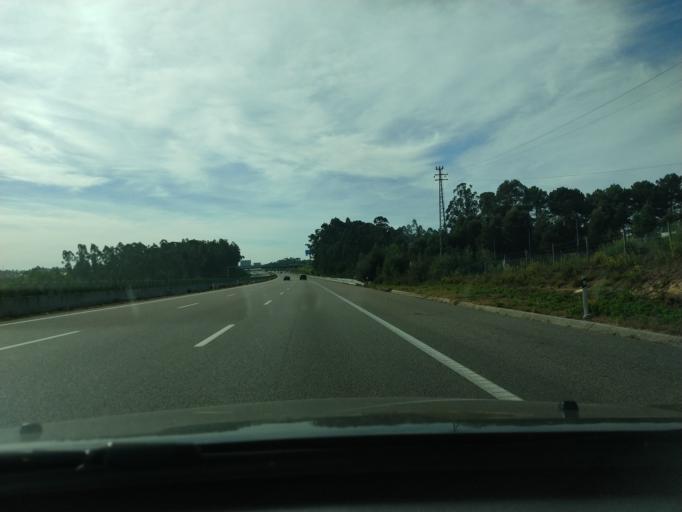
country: PT
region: Aveiro
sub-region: Santa Maria da Feira
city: Feira
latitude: 40.9166
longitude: -8.5680
